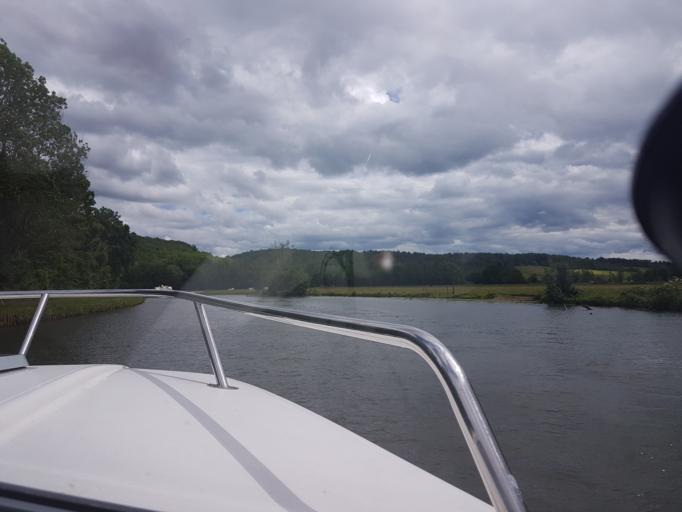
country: FR
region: Bourgogne
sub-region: Departement de l'Yonne
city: Vermenton
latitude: 47.5805
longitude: 3.6479
